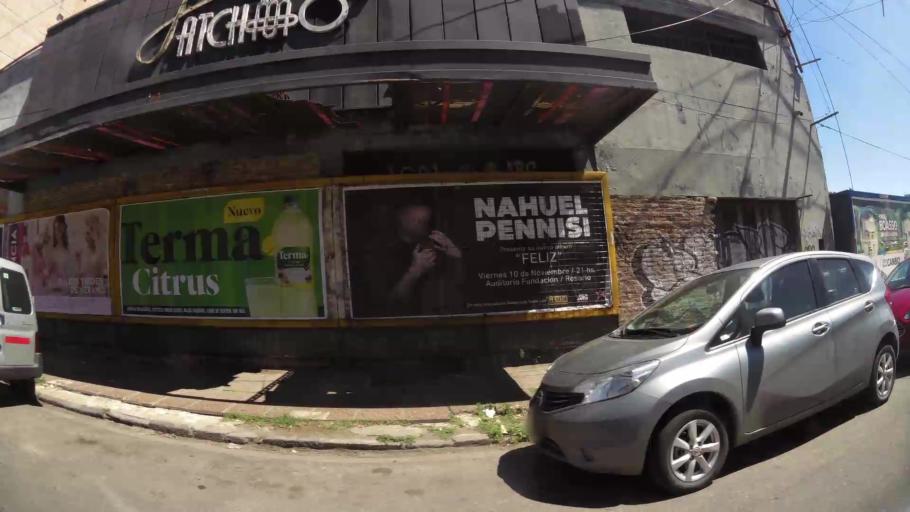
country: AR
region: Santa Fe
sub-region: Departamento de Rosario
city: Rosario
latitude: -32.9313
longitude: -60.6551
